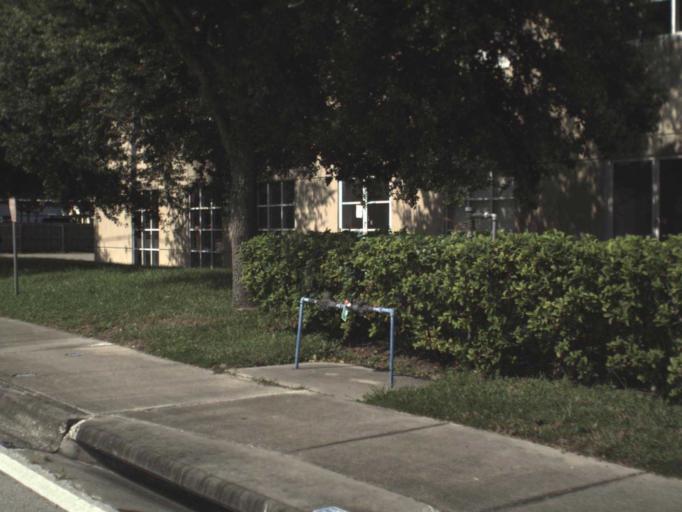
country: US
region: Florida
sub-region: Hillsborough County
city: Lake Magdalene
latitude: 28.1022
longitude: -82.4606
